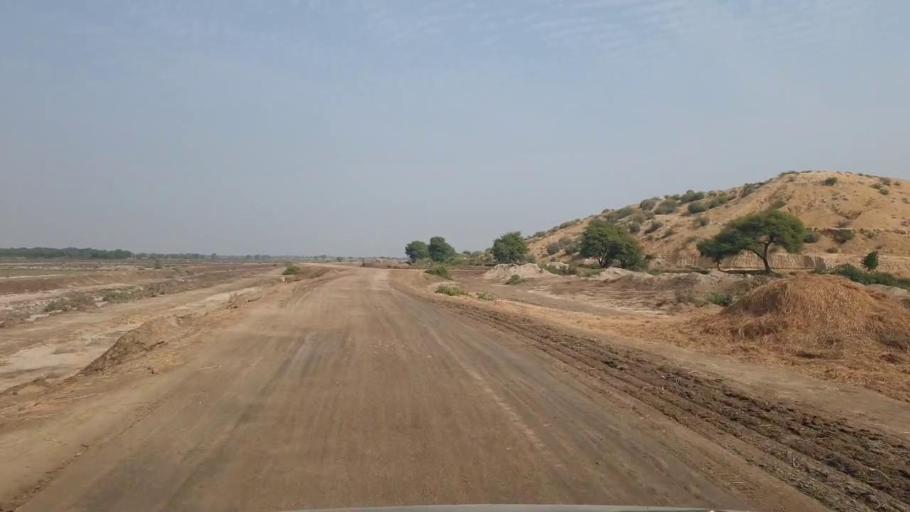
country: PK
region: Sindh
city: Tando Muhammad Khan
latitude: 25.1456
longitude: 68.4584
